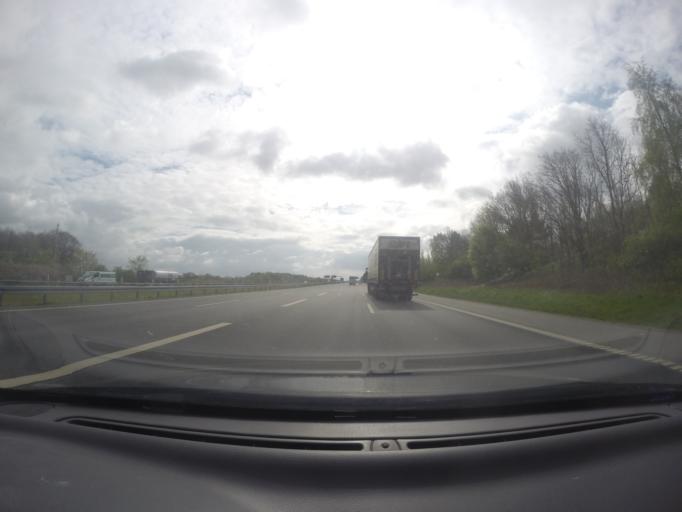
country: DK
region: Capital Region
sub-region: Ballerup Kommune
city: Ballerup
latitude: 55.6997
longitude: 12.3770
